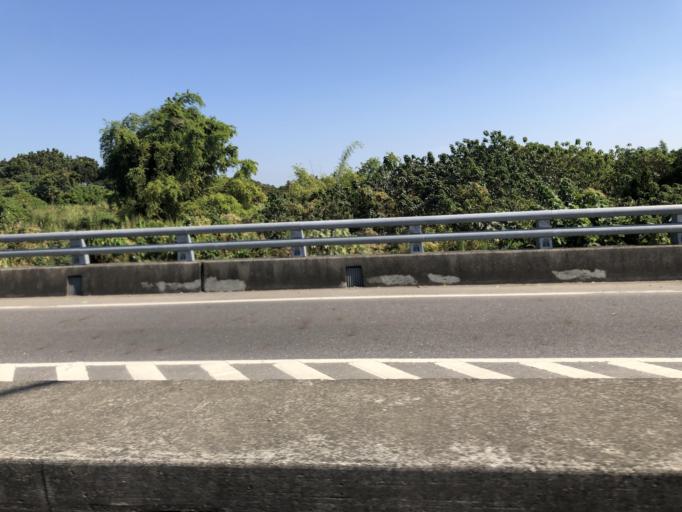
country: TW
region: Taiwan
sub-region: Tainan
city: Tainan
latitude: 23.0349
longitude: 120.3218
